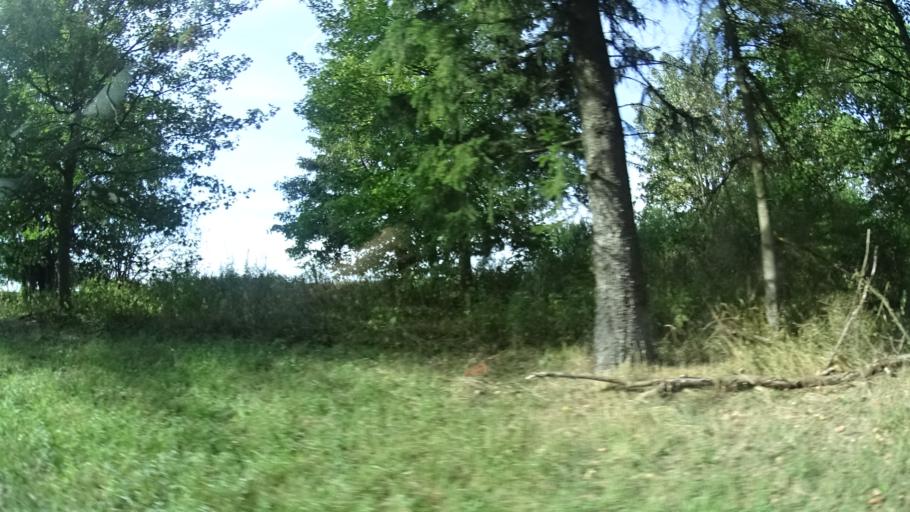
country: DE
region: Thuringia
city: Stepfershausen
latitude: 50.5779
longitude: 10.2724
